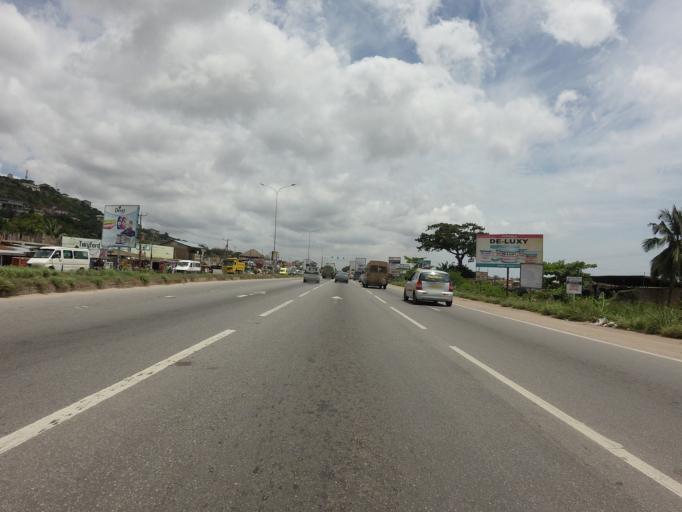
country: GH
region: Greater Accra
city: Gbawe
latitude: 5.5556
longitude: -0.3040
